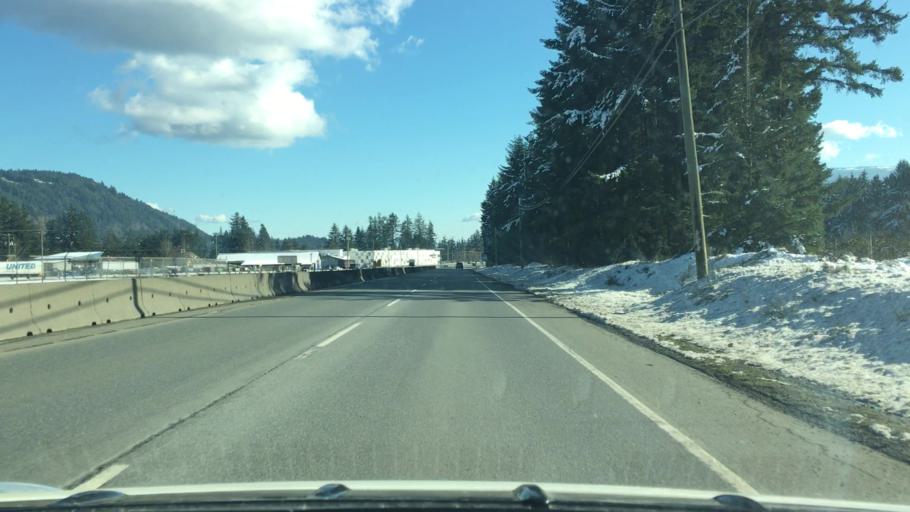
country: CA
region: British Columbia
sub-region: Cowichan Valley Regional District
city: Ladysmith
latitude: 49.0406
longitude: -123.8678
